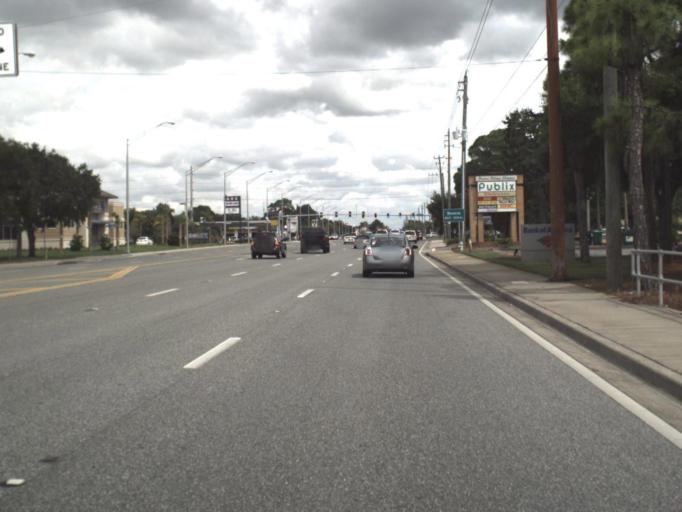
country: US
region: Florida
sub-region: Sarasota County
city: South Gate Ridge
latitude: 27.2692
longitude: -82.5003
